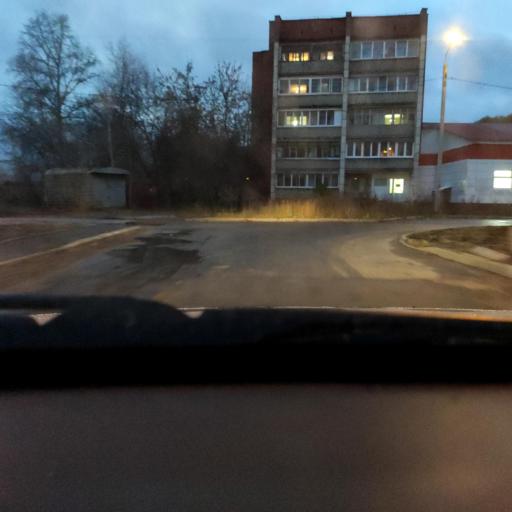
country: RU
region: Perm
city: Kondratovo
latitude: 58.0388
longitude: 56.1126
